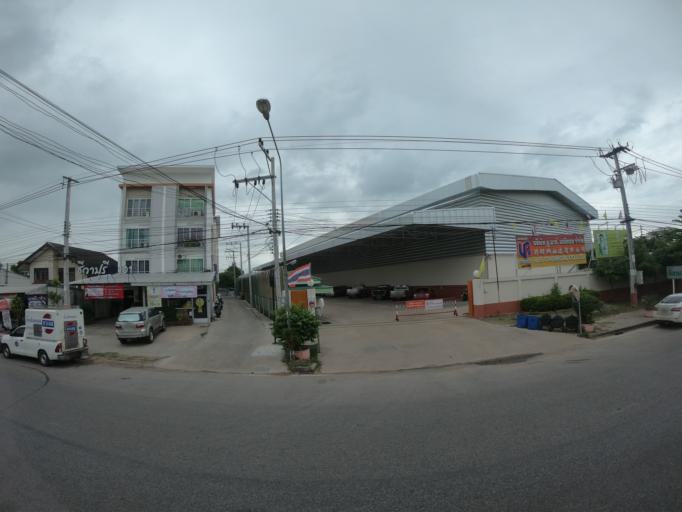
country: TH
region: Roi Et
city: Roi Et
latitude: 16.0463
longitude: 103.6364
